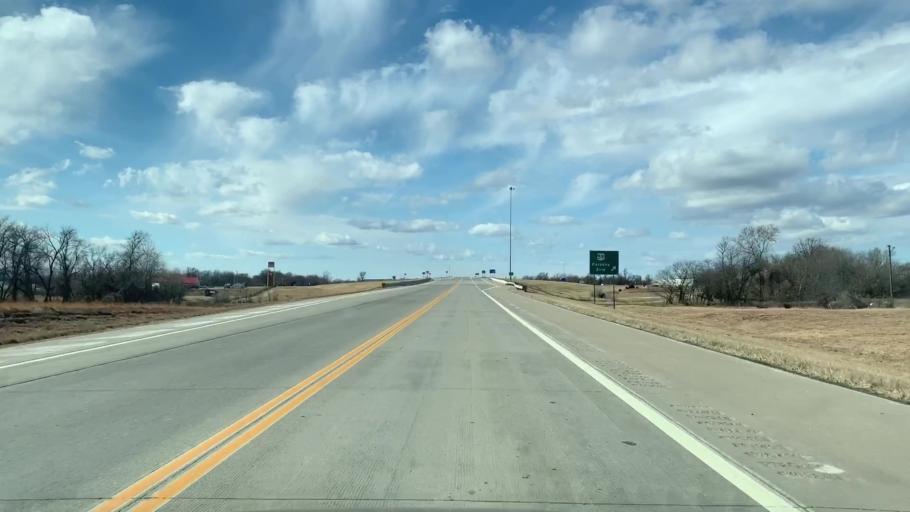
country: US
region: Kansas
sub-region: Labette County
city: Parsons
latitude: 37.3656
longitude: -95.2512
